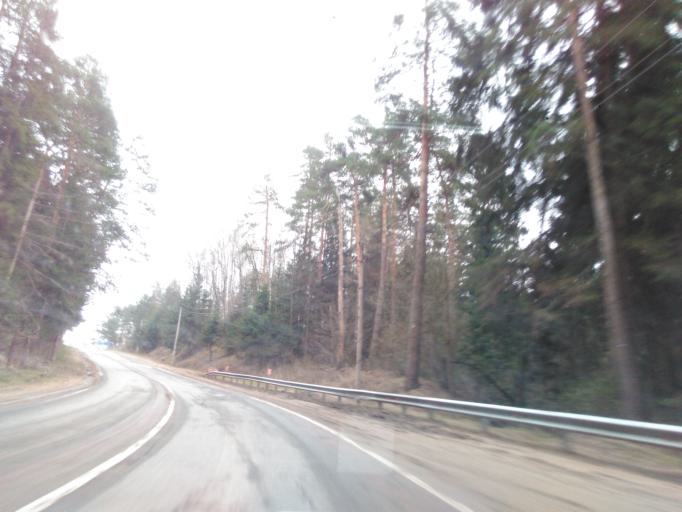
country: RU
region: Moskovskaya
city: Snegiri
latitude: 55.8421
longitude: 36.9629
